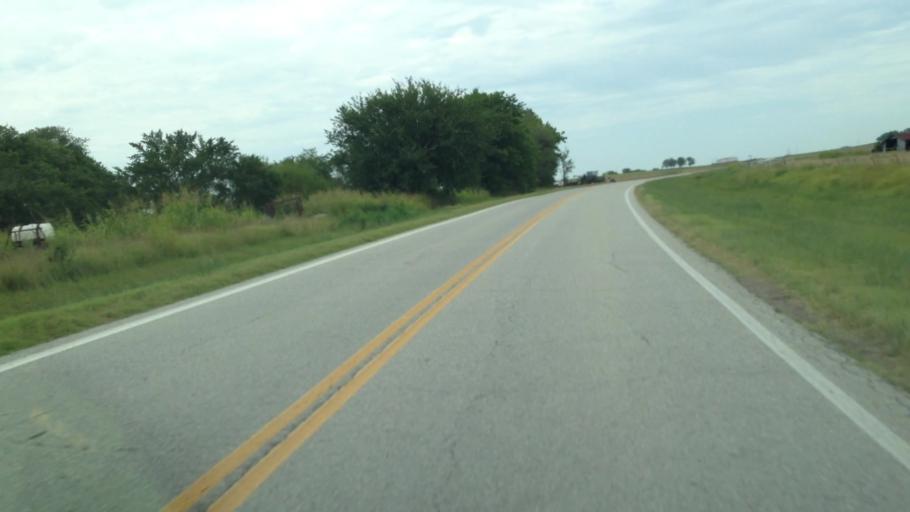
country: US
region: Oklahoma
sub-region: Craig County
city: Vinita
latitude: 36.8215
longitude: -95.1430
